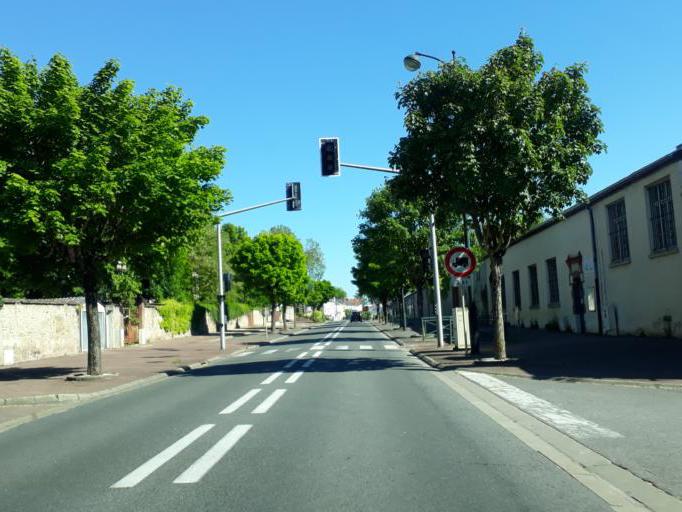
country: FR
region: Centre
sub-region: Departement du Loiret
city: Briare
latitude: 47.6449
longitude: 2.7327
